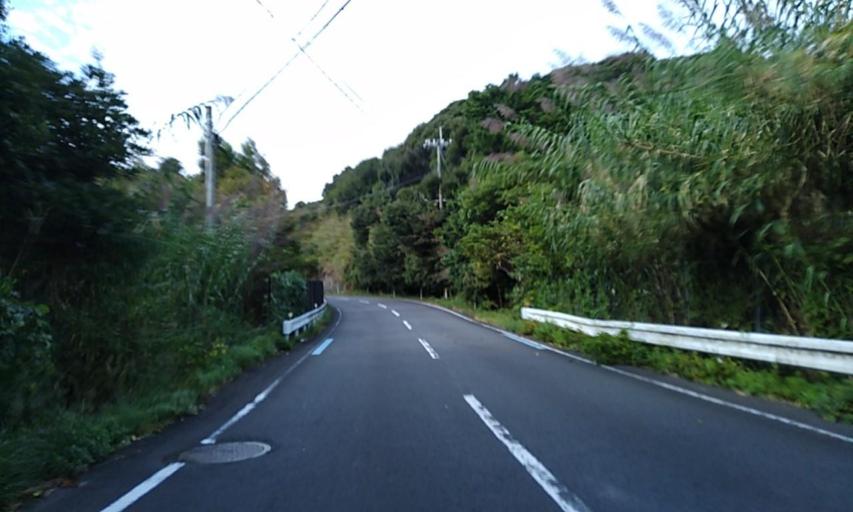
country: JP
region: Wakayama
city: Shingu
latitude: 33.4699
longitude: 135.8206
